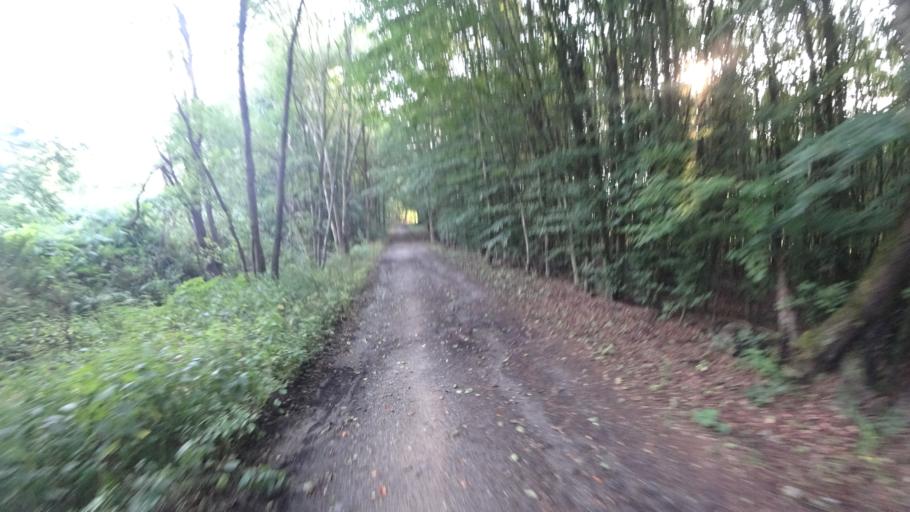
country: DE
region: Rheinland-Pfalz
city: Hohr-Grenzhausen
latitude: 50.4363
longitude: 7.6428
